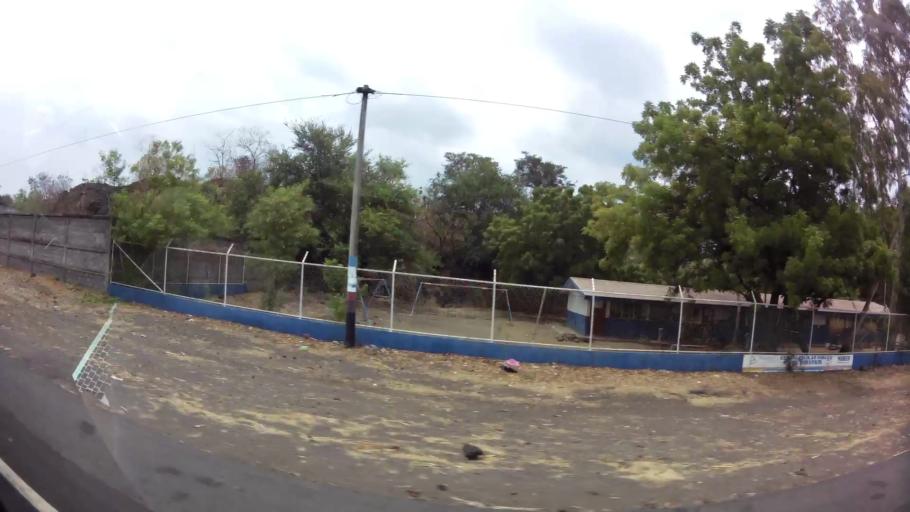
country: NI
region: Leon
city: Quezalguaque
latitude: 12.5317
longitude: -86.8926
